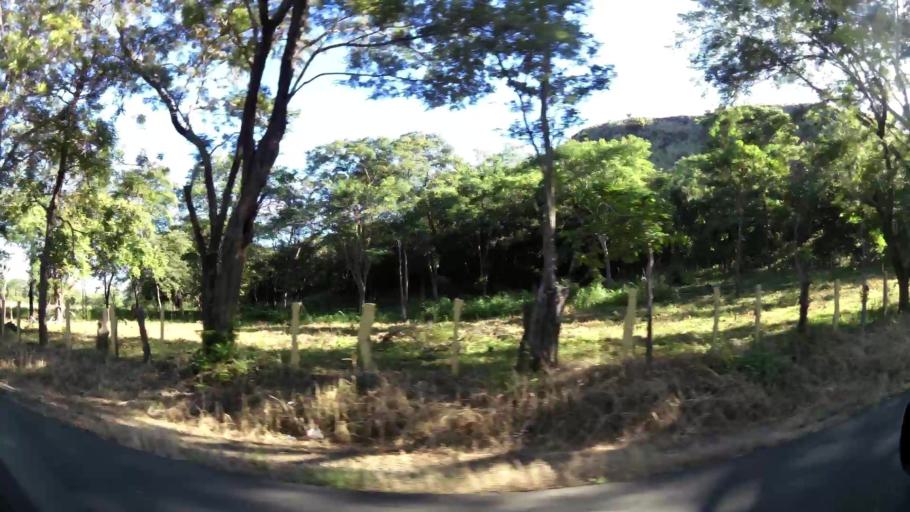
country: CR
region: Guanacaste
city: Sardinal
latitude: 10.5018
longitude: -85.6446
